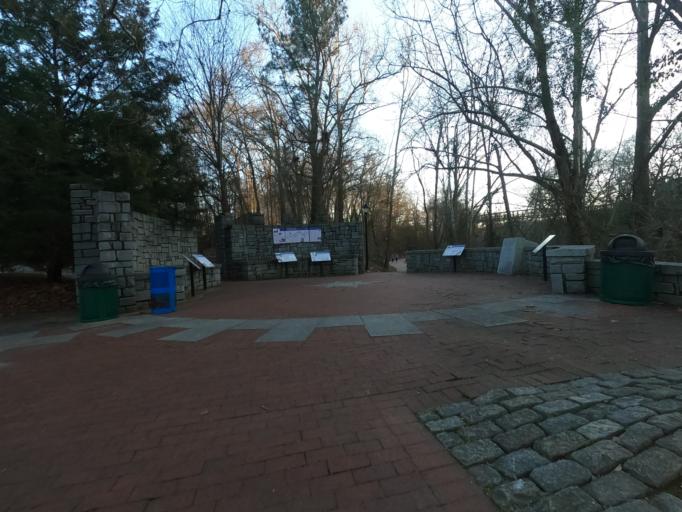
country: US
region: Georgia
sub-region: Clarke County
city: Athens
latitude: 33.9578
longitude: -83.3661
